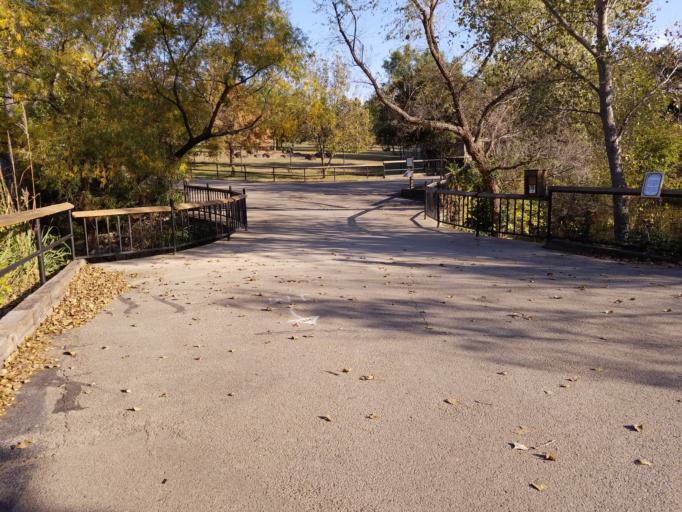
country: US
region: Kansas
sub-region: Saline County
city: Salina
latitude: 38.8535
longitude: -97.7657
